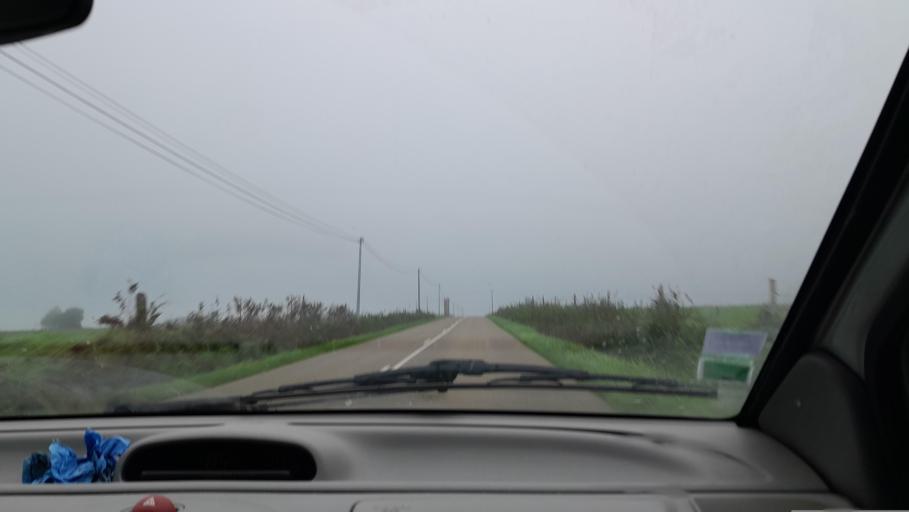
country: FR
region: Brittany
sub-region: Departement d'Ille-et-Vilaine
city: Le Pertre
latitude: 47.9965
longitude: -0.9788
